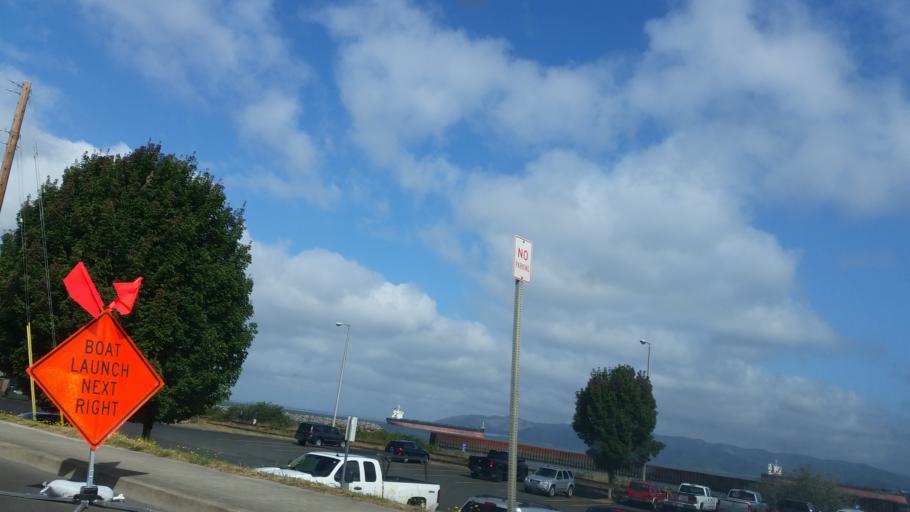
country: US
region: Oregon
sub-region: Clatsop County
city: Astoria
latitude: 46.1935
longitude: -123.8034
